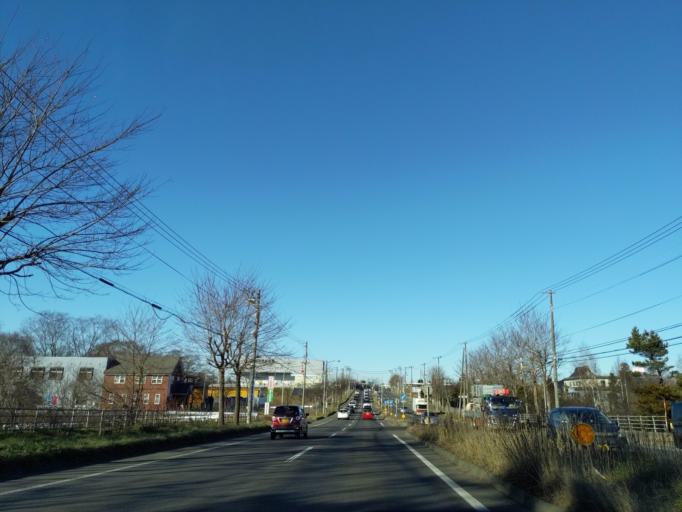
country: JP
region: Hokkaido
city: Kitahiroshima
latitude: 42.9484
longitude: 141.4991
